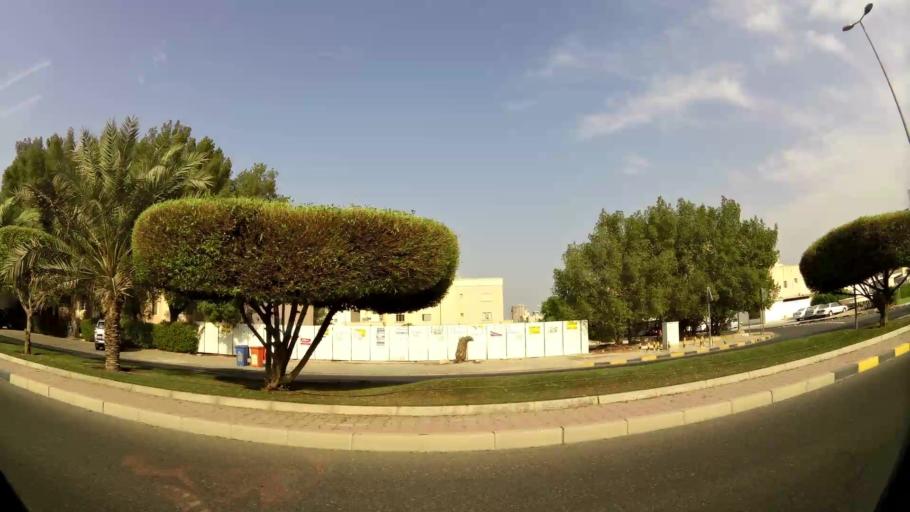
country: KW
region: Al Asimah
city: Ad Dasmah
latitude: 29.3363
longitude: 47.9957
